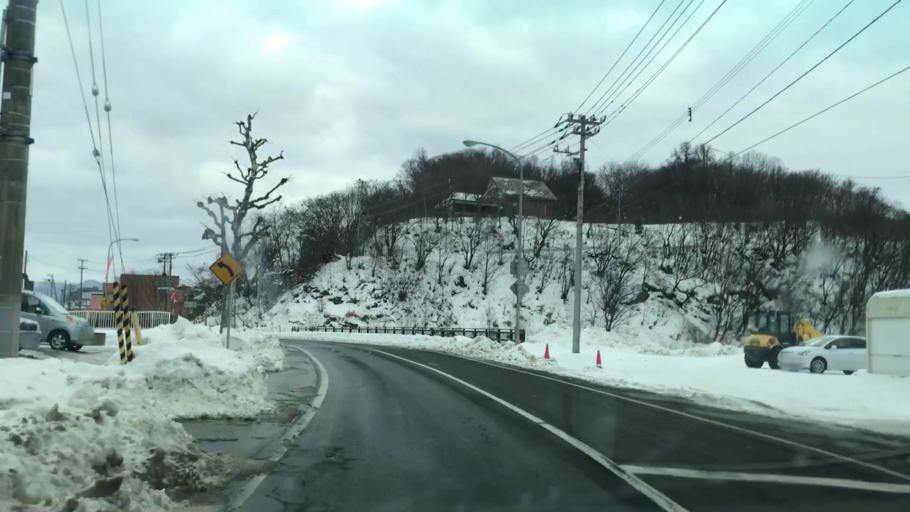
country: JP
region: Hokkaido
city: Yoichi
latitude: 43.2023
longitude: 140.7735
